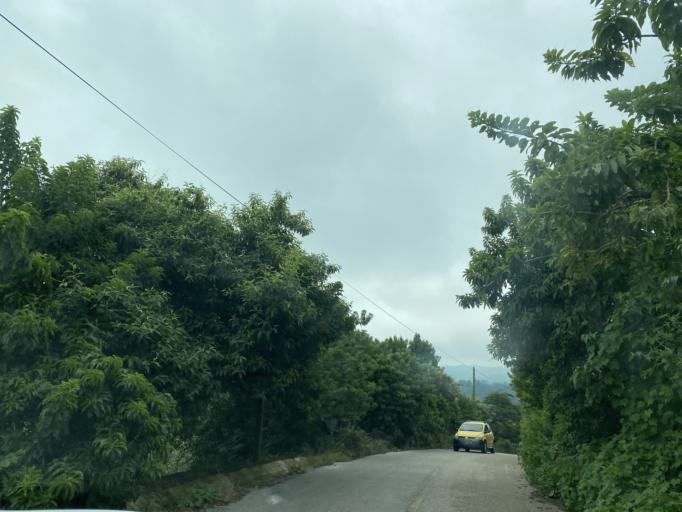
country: MX
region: Morelos
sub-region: Yecapixtla
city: Achichipico
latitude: 18.9552
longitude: -98.8304
